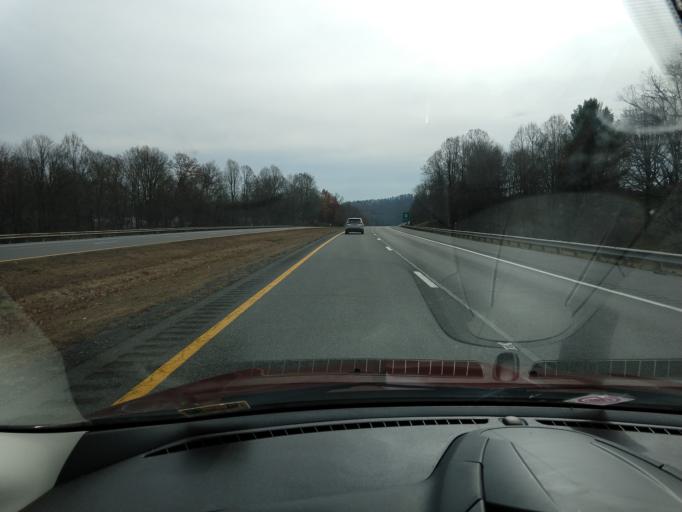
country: US
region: West Virginia
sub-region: Nicholas County
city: Summersville
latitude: 38.2854
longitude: -80.8328
